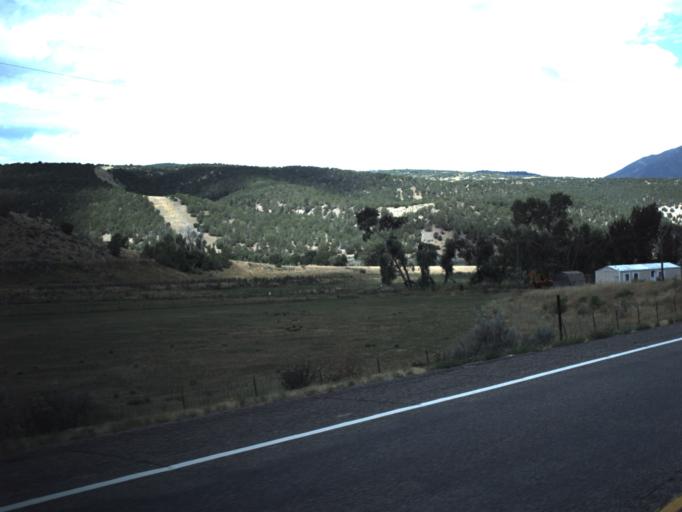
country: US
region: Utah
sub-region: Utah County
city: Woodland Hills
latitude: 39.8843
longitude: -111.5460
